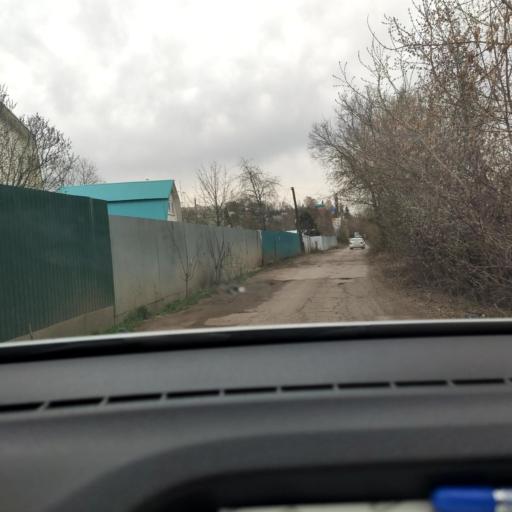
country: RU
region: Bashkortostan
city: Avdon
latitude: 54.6259
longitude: 55.5948
